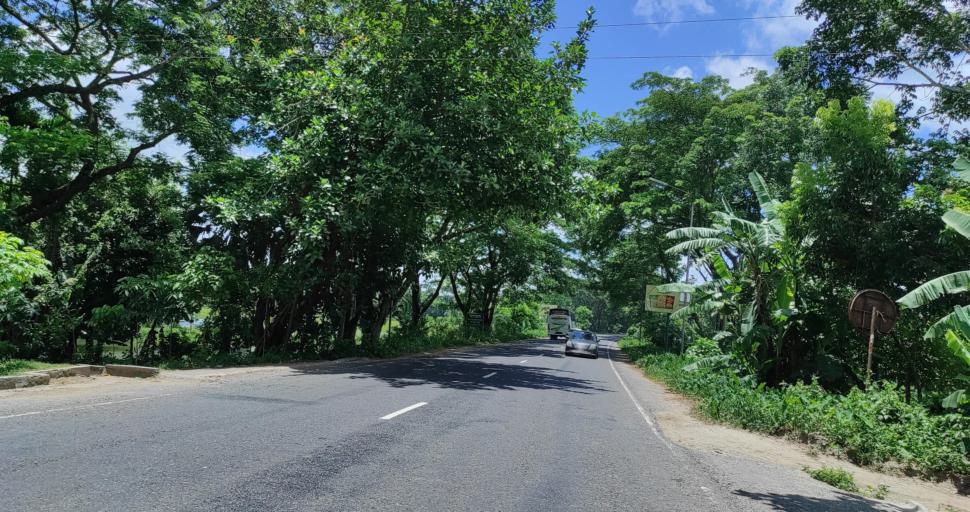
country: BD
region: Barisal
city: Barisal
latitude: 22.8219
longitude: 90.2674
